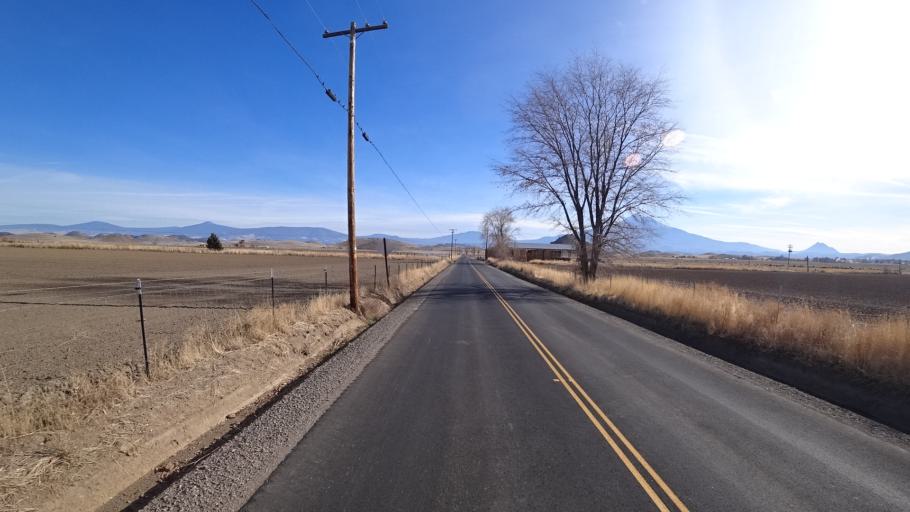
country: US
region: California
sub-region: Siskiyou County
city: Weed
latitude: 41.5381
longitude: -122.5366
